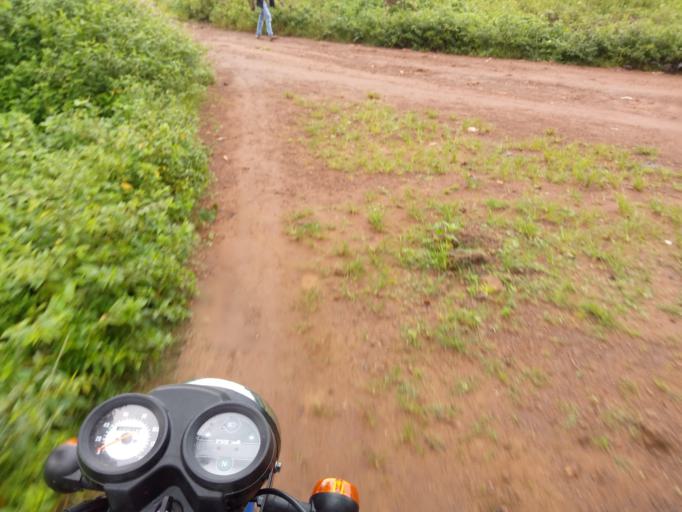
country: SL
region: Eastern Province
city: Buedu
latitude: 8.4641
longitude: -10.3406
